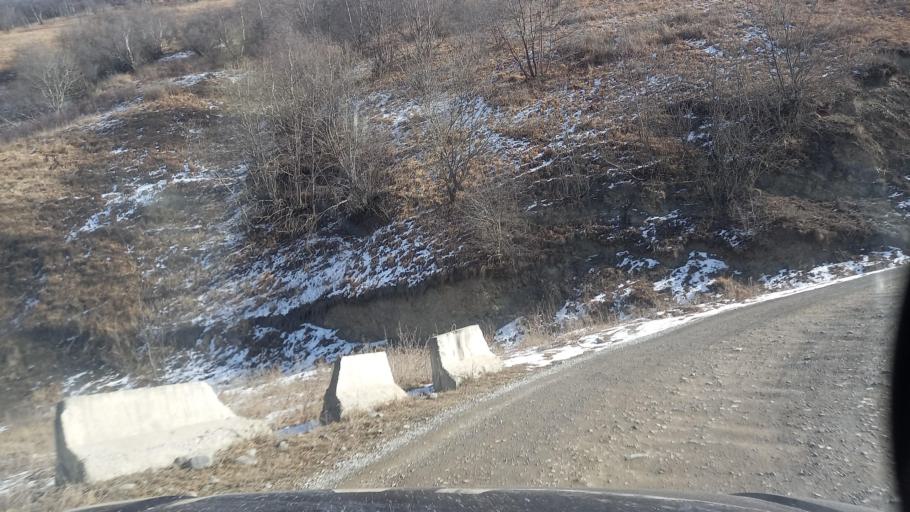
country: RU
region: North Ossetia
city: Verkhniy Fiagdon
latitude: 42.8399
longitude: 44.4647
